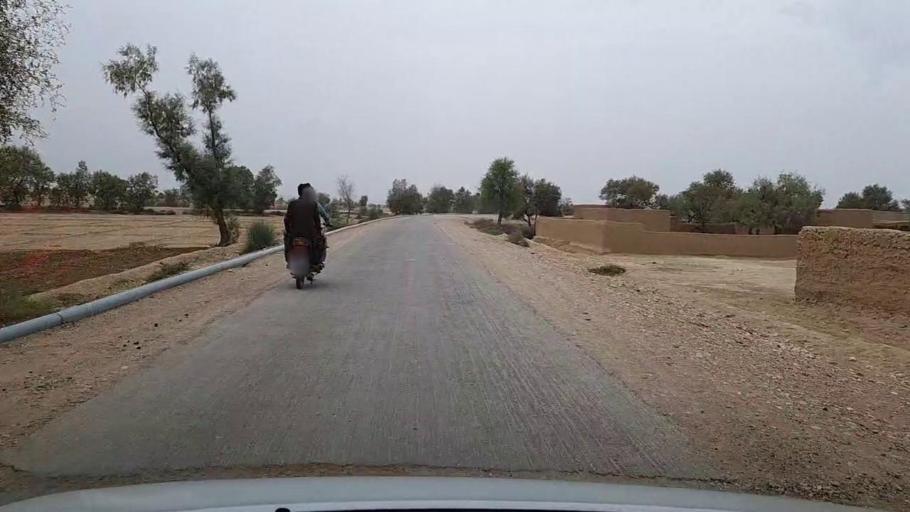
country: PK
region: Sindh
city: Sehwan
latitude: 26.3221
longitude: 67.7287
